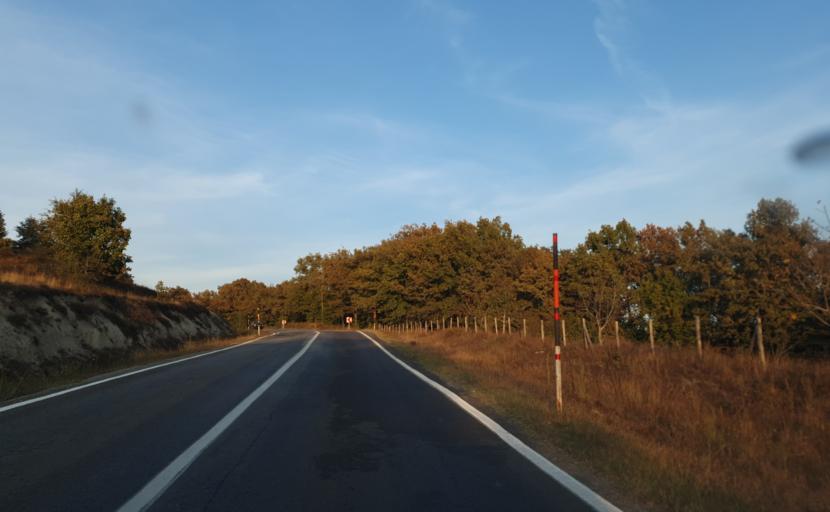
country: TR
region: Kirklareli
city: Sergen
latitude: 41.8392
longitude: 27.7972
